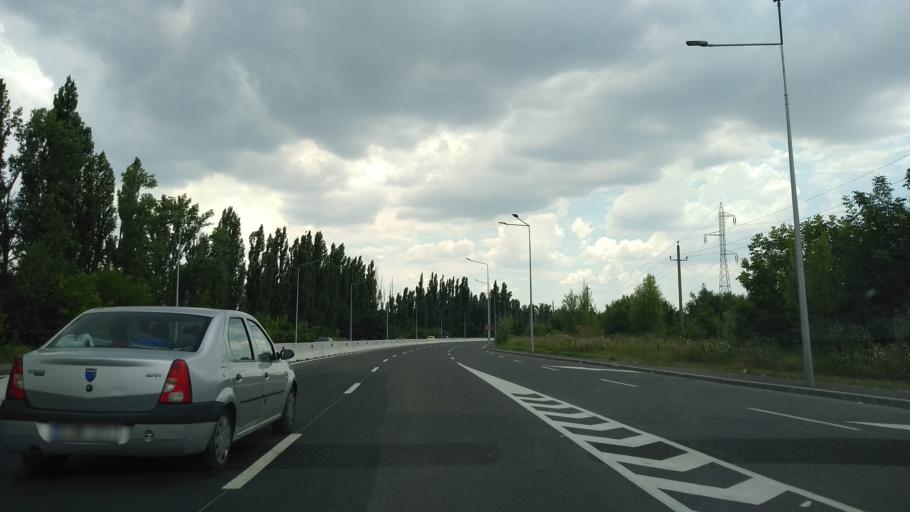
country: RO
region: Ilfov
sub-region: Comuna Popesti-Leordeni
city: Popesti-Leordeni
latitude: 44.3962
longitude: 26.1581
